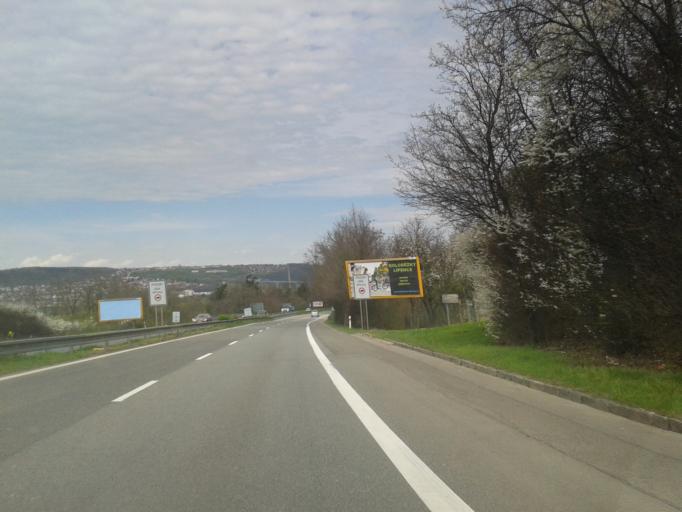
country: CZ
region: Central Bohemia
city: Vrane nad Vltavou
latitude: 49.9674
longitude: 14.3762
